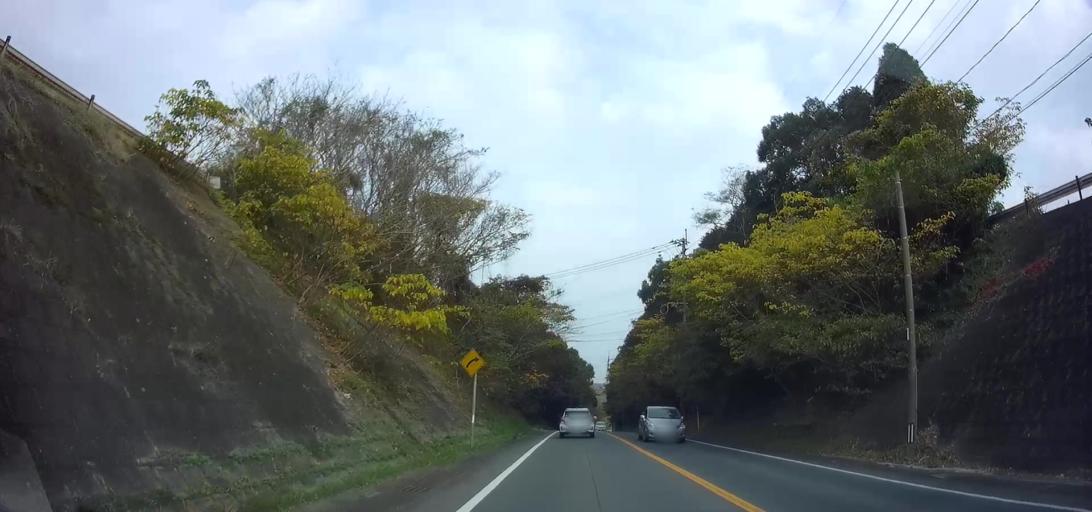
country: JP
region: Nagasaki
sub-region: Isahaya-shi
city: Isahaya
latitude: 32.7876
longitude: 130.0461
